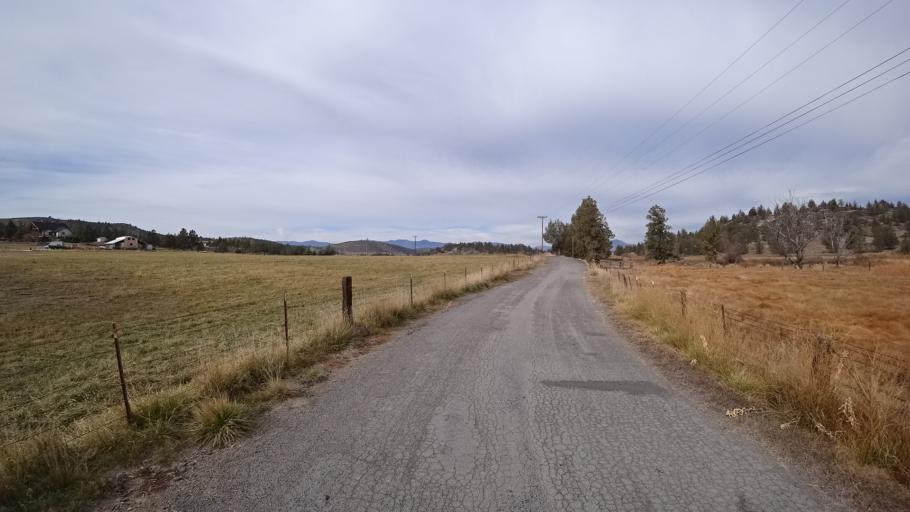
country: US
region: California
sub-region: Siskiyou County
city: Montague
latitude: 41.6827
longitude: -122.5174
